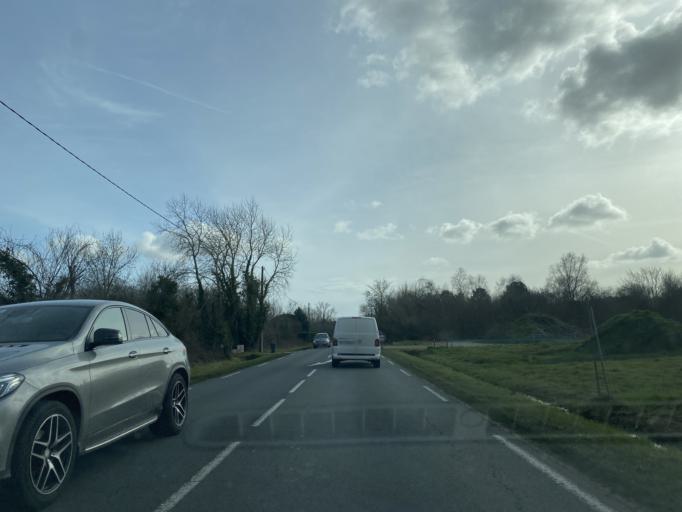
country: FR
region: Aquitaine
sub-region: Departement de la Gironde
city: Le Taillan-Medoc
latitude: 44.9261
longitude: -0.6773
